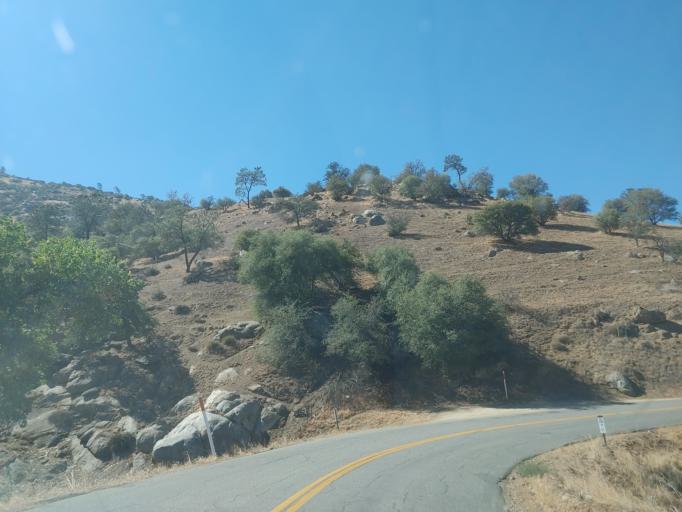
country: US
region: California
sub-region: Kern County
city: Golden Hills
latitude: 35.1806
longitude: -118.5151
